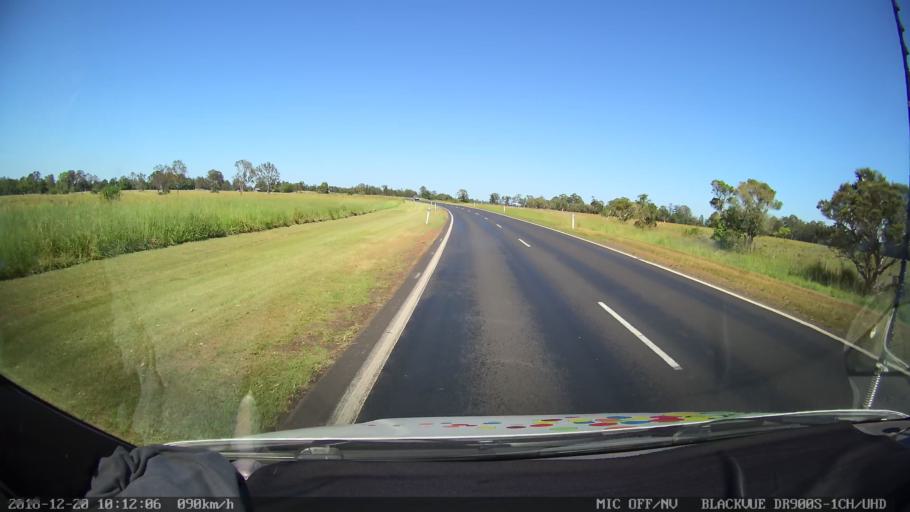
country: AU
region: New South Wales
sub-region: Richmond Valley
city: Casino
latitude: -28.8717
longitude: 153.1487
